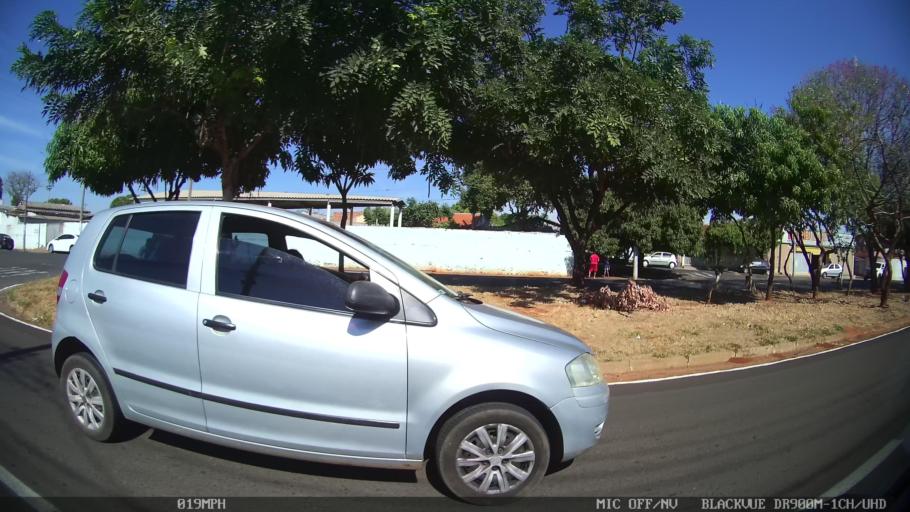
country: BR
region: Sao Paulo
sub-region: Sao Jose Do Rio Preto
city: Sao Jose do Rio Preto
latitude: -20.7770
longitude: -49.4063
